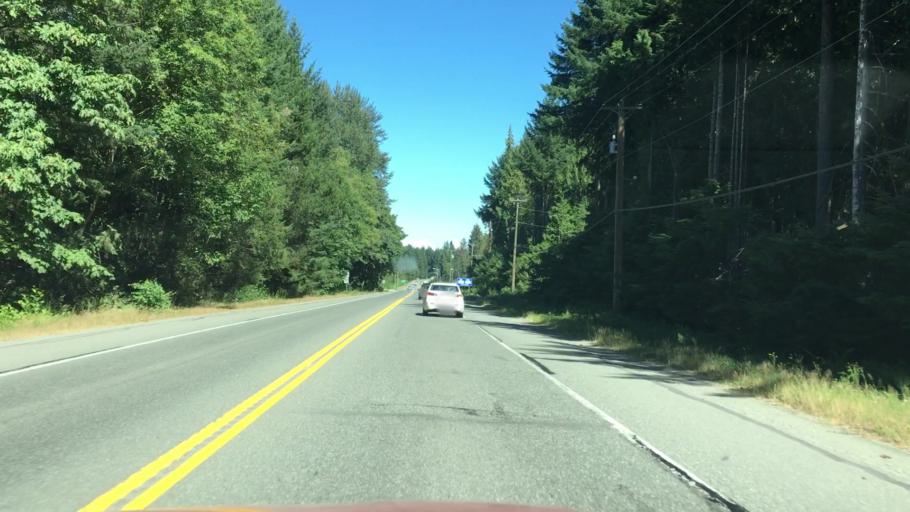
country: CA
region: British Columbia
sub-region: Regional District of Nanaimo
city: Parksville
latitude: 49.3110
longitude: -124.5229
